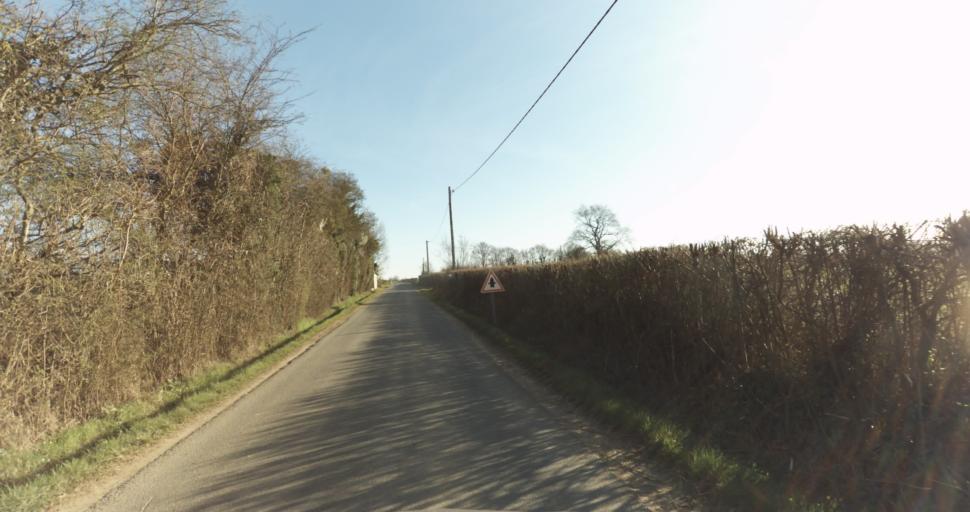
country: FR
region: Lower Normandy
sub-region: Departement de l'Orne
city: Trun
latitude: 48.9305
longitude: 0.0302
